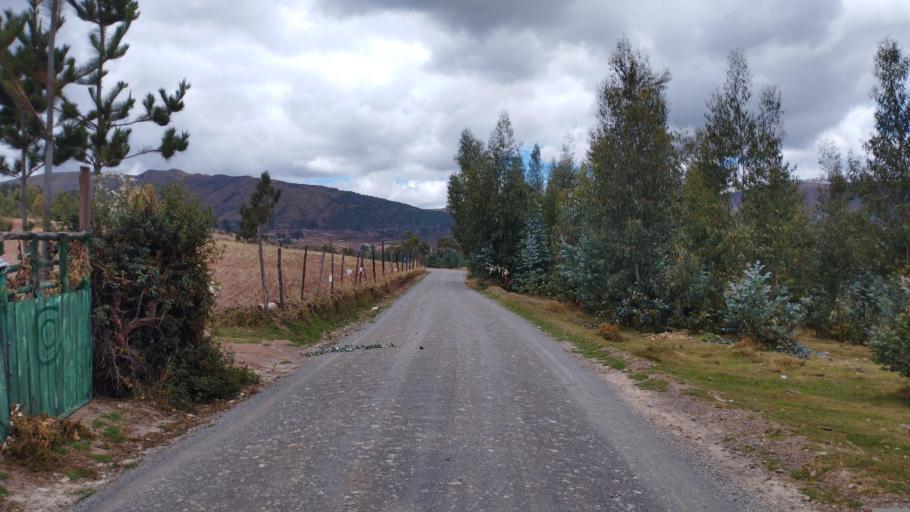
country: PE
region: Cusco
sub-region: Provincia de Cusco
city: Cusco
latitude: -13.5110
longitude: -71.9419
